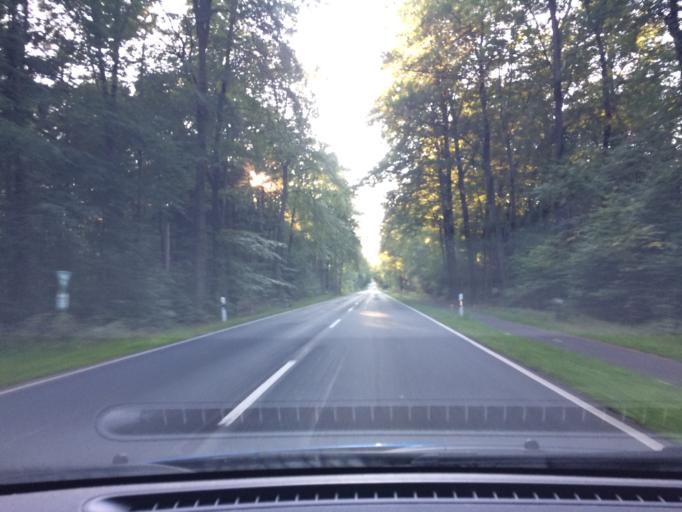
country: DE
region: Lower Saxony
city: Unterluss
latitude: 52.8192
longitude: 10.3352
